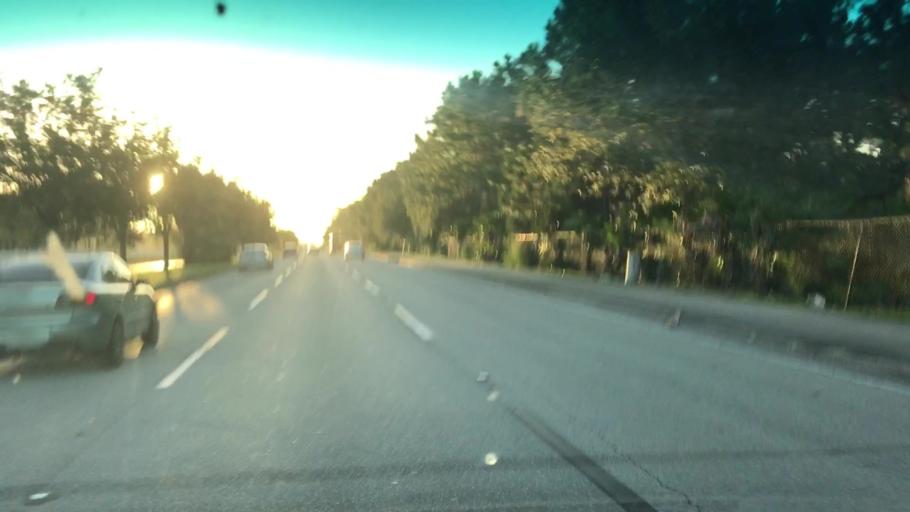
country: US
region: Florida
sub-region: Lee County
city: Villas
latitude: 26.5460
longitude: -81.8806
